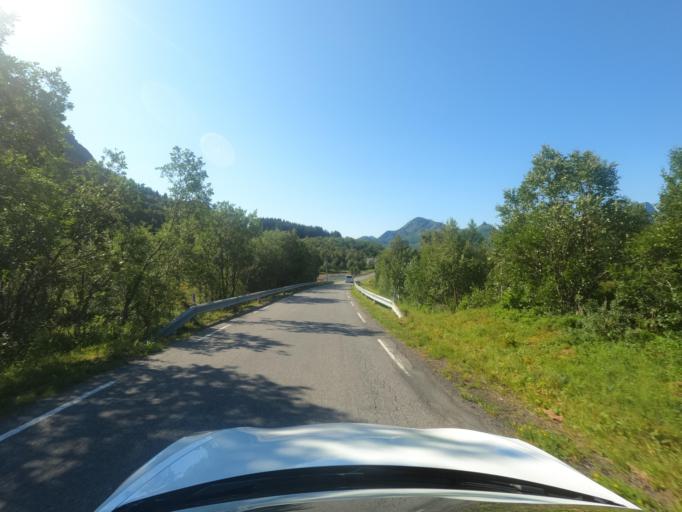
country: NO
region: Nordland
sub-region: Hadsel
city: Stokmarknes
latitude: 68.3205
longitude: 15.0038
